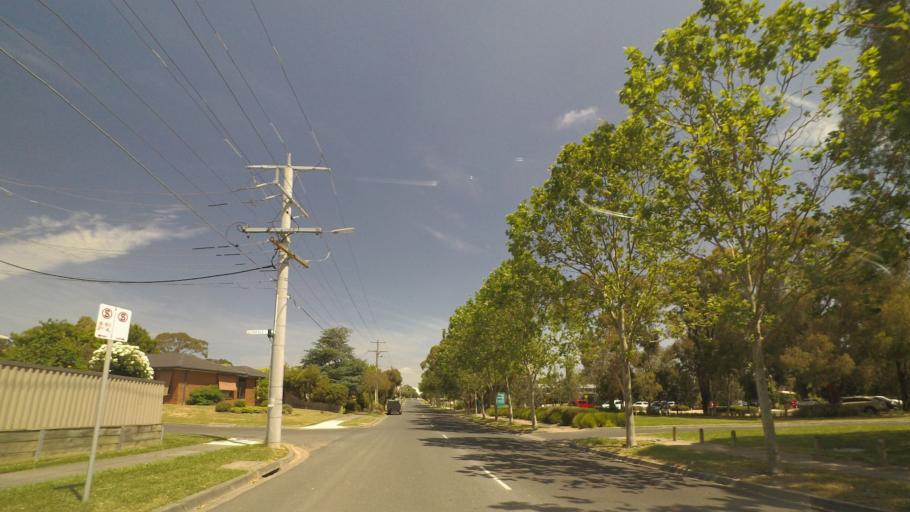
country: AU
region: Victoria
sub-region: Yarra Ranges
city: Chirnside Park
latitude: -37.7526
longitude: 145.3109
